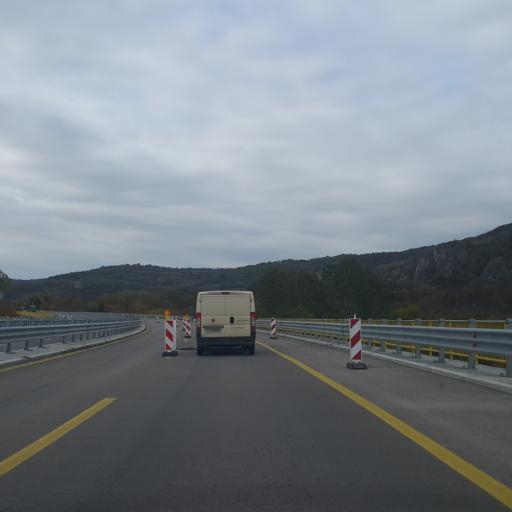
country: RS
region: Central Serbia
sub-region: Pirotski Okrug
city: Bela Palanka
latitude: 43.2342
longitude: 22.3756
